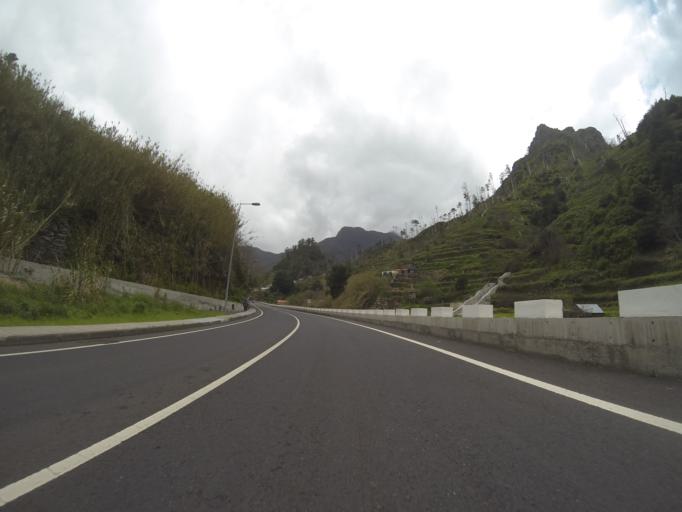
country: PT
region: Madeira
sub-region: Camara de Lobos
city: Curral das Freiras
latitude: 32.7304
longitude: -17.0210
